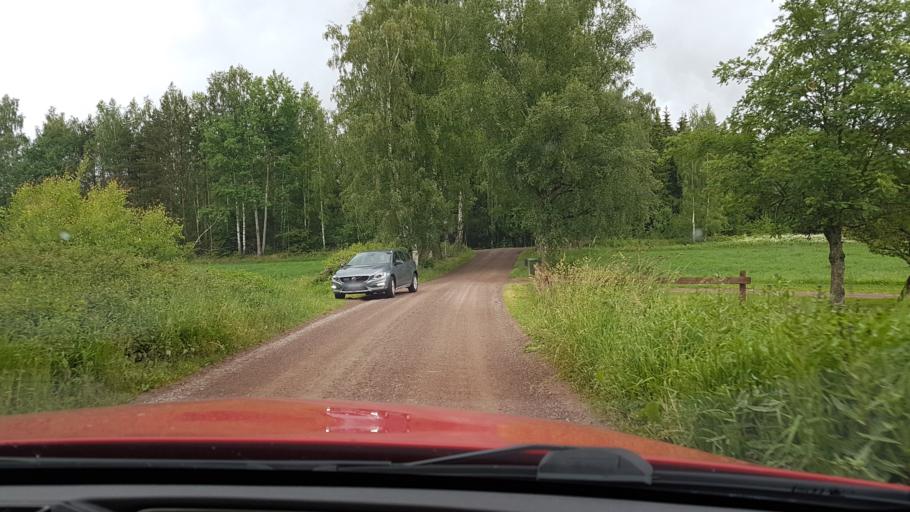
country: SE
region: Vaestra Goetaland
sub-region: Tibro Kommun
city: Tibro
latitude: 58.4282
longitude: 14.1253
